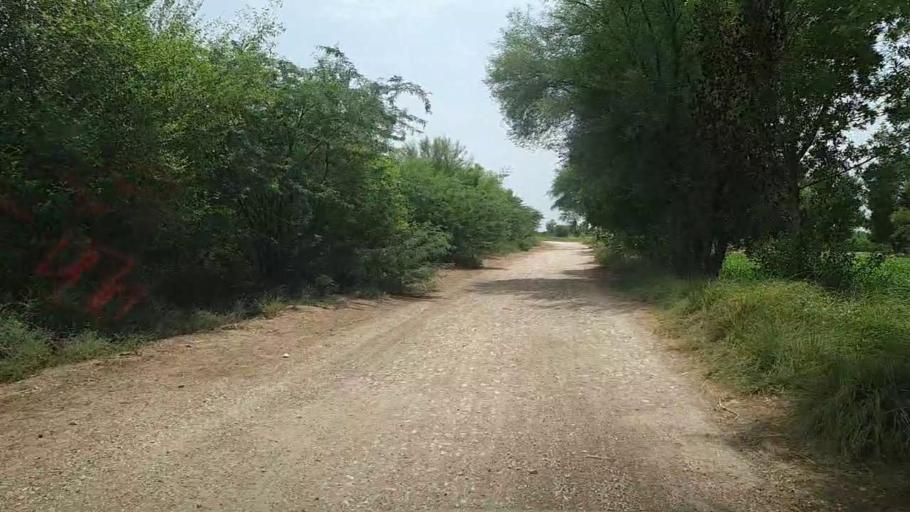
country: PK
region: Sindh
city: Karaundi
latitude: 26.9085
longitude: 68.3216
